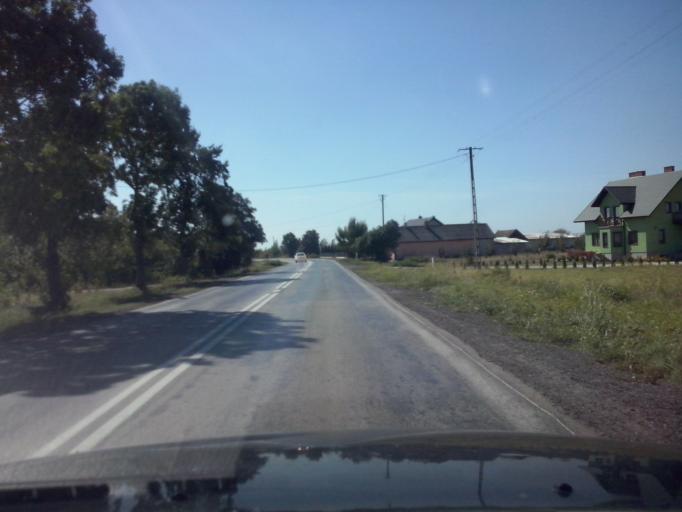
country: PL
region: Swietokrzyskie
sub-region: Powiat staszowski
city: Szydlow
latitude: 50.6117
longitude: 21.0091
